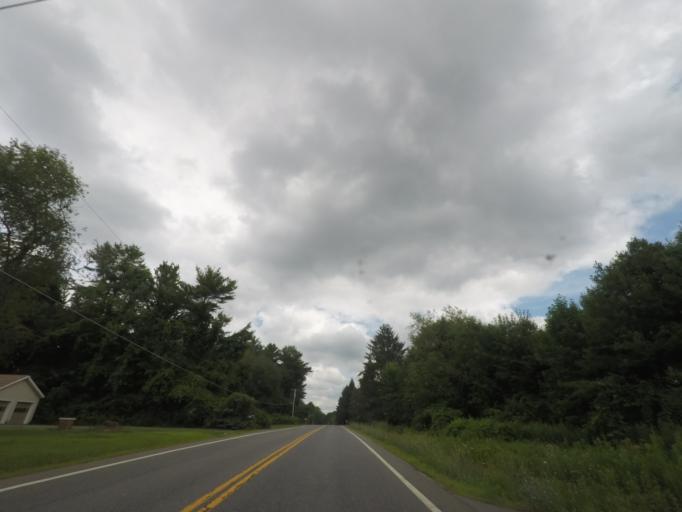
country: US
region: New York
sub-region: Saratoga County
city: Stillwater
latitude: 42.9966
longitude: -73.7123
